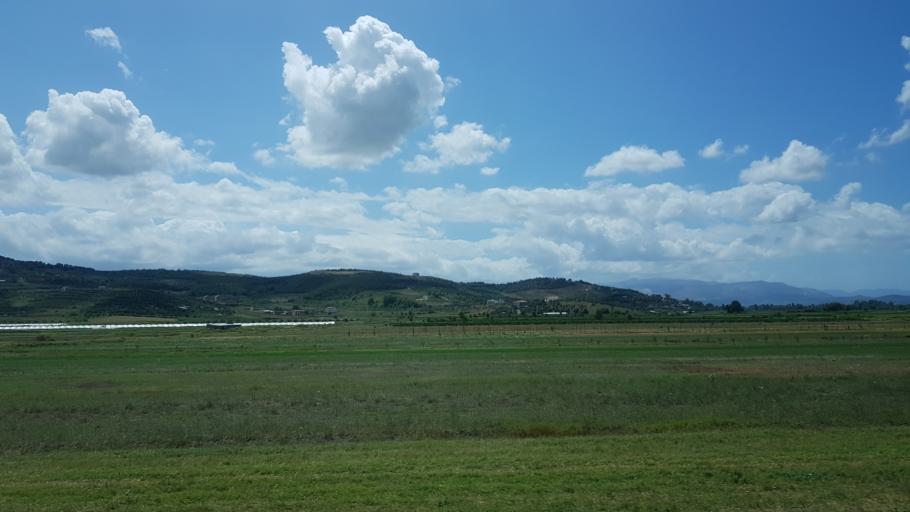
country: AL
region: Fier
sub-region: Rrethi i Fierit
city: Cakran
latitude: 40.5945
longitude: 19.5835
